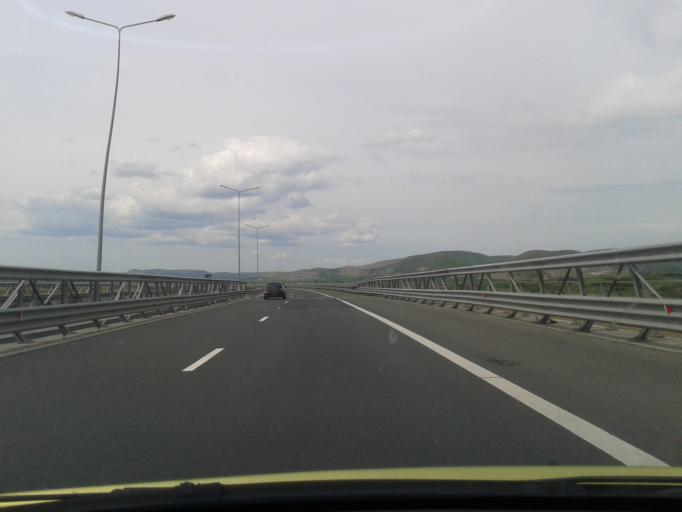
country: RO
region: Hunedoara
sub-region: Oras Simeria
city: Simeria
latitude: 45.8662
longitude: 23.0236
